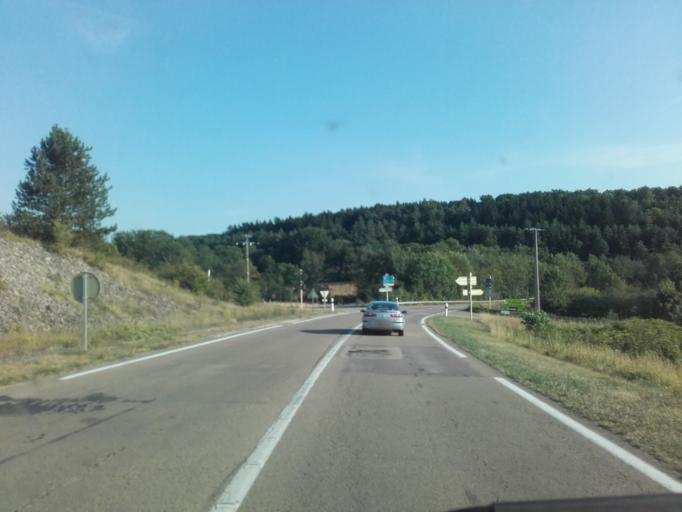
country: FR
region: Bourgogne
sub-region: Departement de l'Yonne
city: Venoy
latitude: 47.8039
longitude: 3.6674
